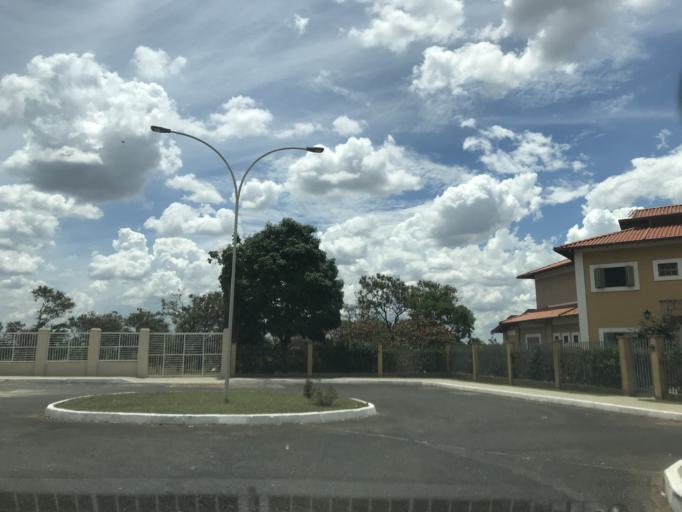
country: BR
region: Federal District
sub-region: Brasilia
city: Brasilia
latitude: -15.8940
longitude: -47.9142
